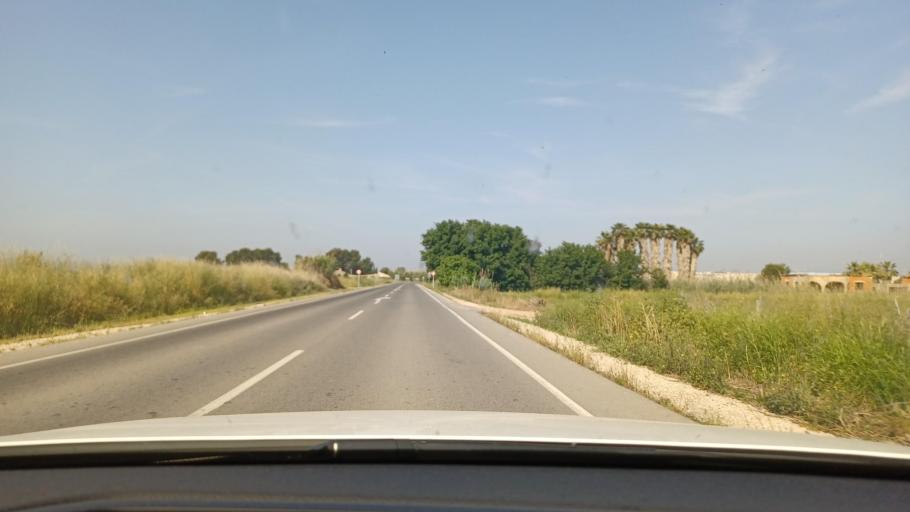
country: ES
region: Valencia
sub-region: Provincia de Alicante
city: Dolores
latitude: 38.1435
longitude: -0.7329
